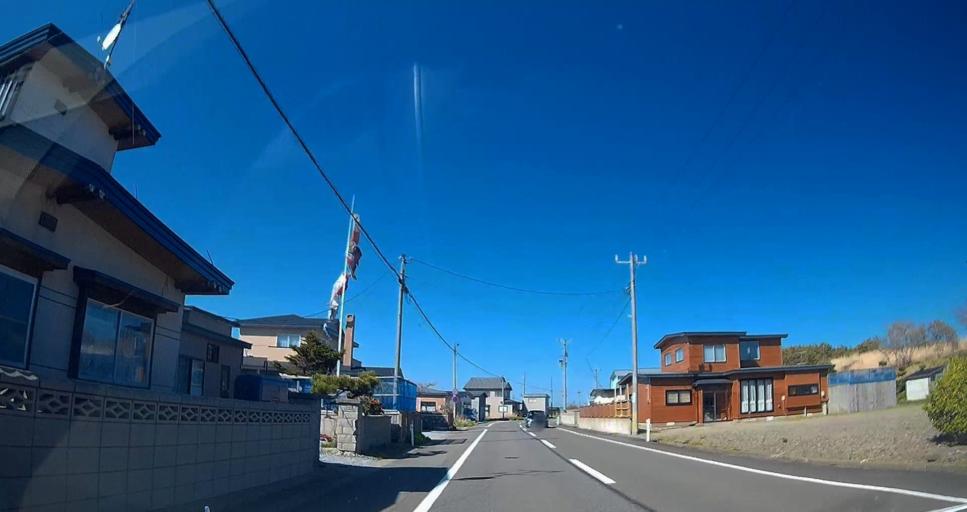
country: JP
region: Hokkaido
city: Hakodate
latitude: 41.5388
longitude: 140.9100
